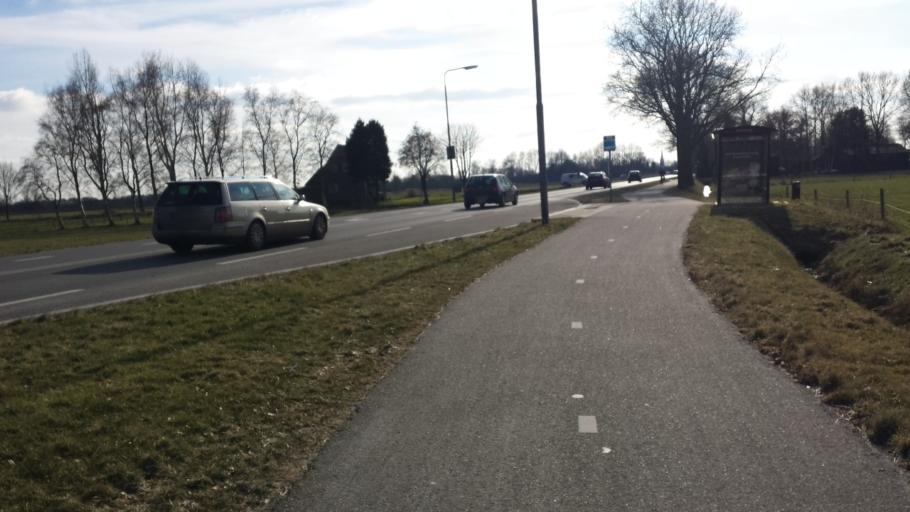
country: NL
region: Overijssel
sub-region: Gemeente Steenwijkerland
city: Steenwijk
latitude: 52.8120
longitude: 6.1349
